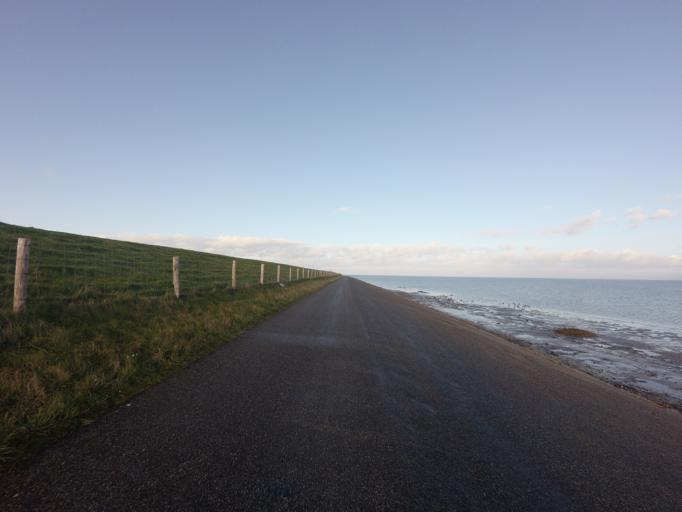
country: NL
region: North Holland
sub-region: Gemeente Texel
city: Den Burg
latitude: 53.1450
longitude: 4.8986
